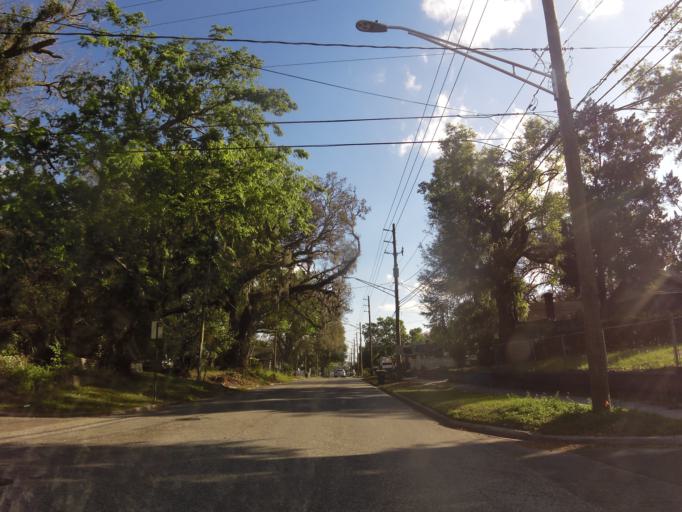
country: US
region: Florida
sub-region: Duval County
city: Jacksonville
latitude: 30.3270
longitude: -81.6909
